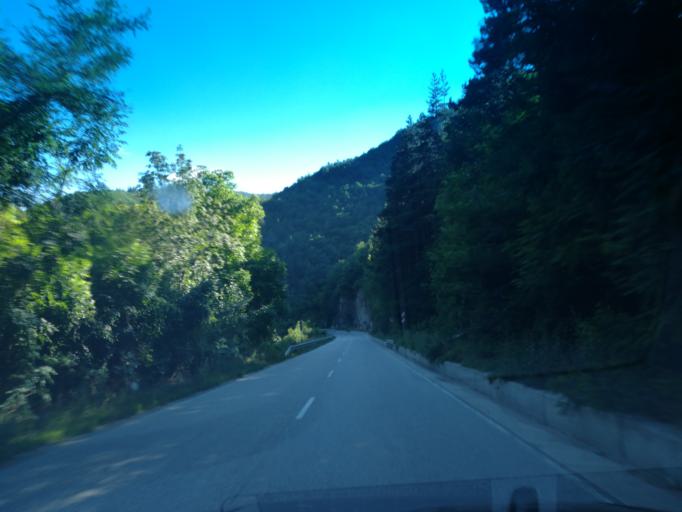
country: BG
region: Smolyan
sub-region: Obshtina Chepelare
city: Chepelare
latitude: 41.7923
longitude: 24.7098
